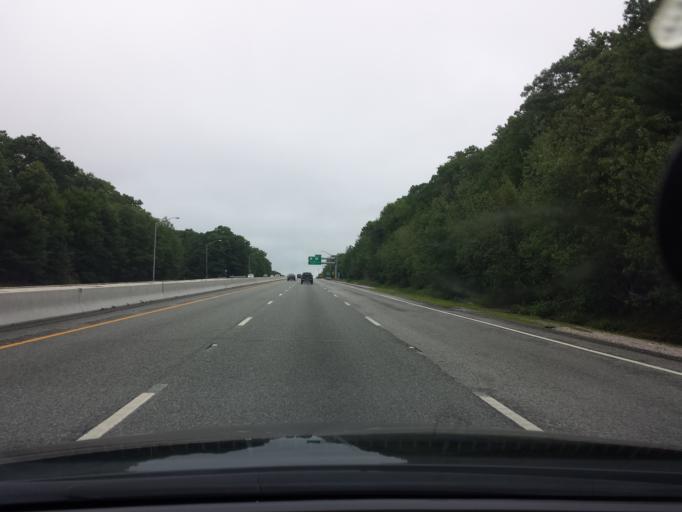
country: US
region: Rhode Island
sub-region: Washington County
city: Hope Valley
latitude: 41.5335
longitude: -71.6806
